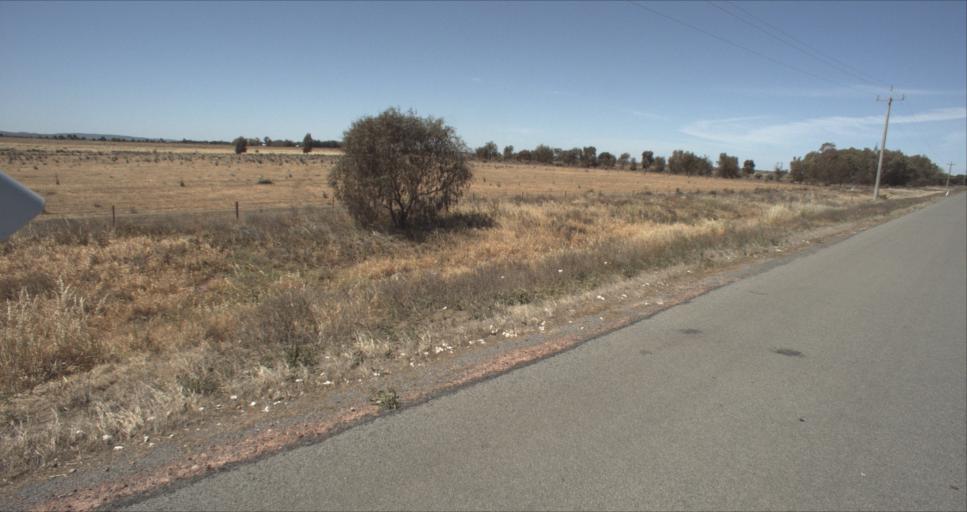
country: AU
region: New South Wales
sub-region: Leeton
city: Leeton
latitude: -34.4337
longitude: 146.2991
